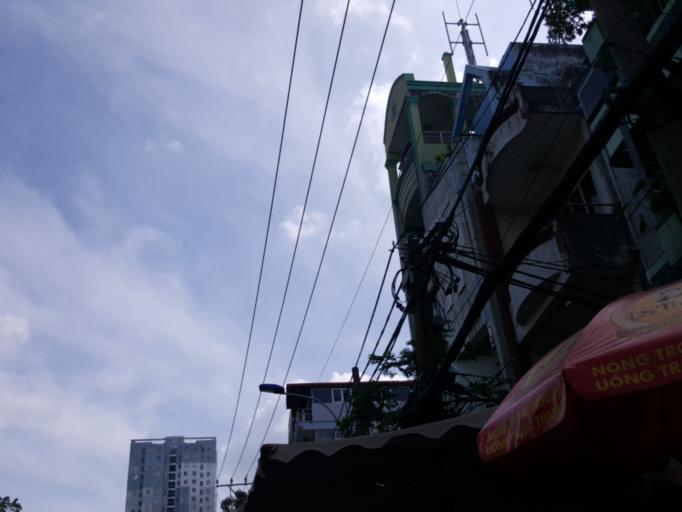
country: VN
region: Ho Chi Minh City
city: Quan Bon
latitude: 10.7636
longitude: 106.7051
